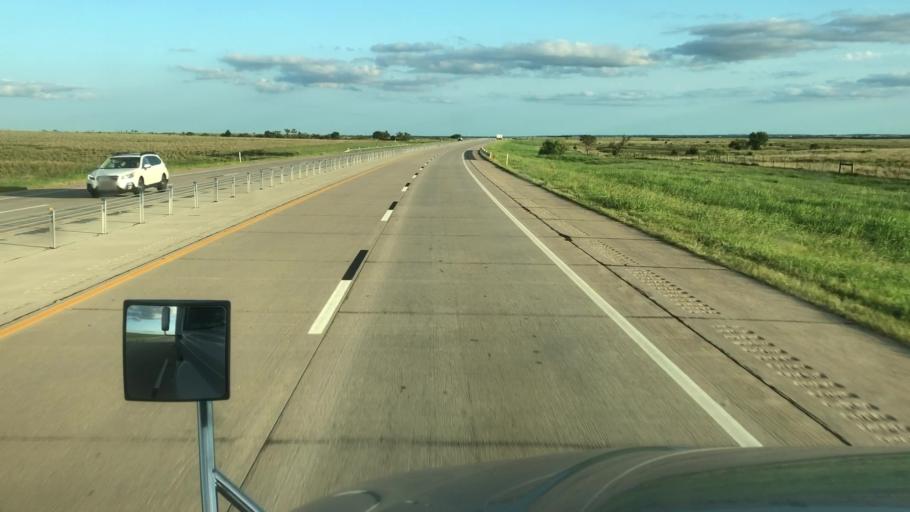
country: US
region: Oklahoma
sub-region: Pawnee County
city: Pawnee
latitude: 36.3671
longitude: -97.0354
